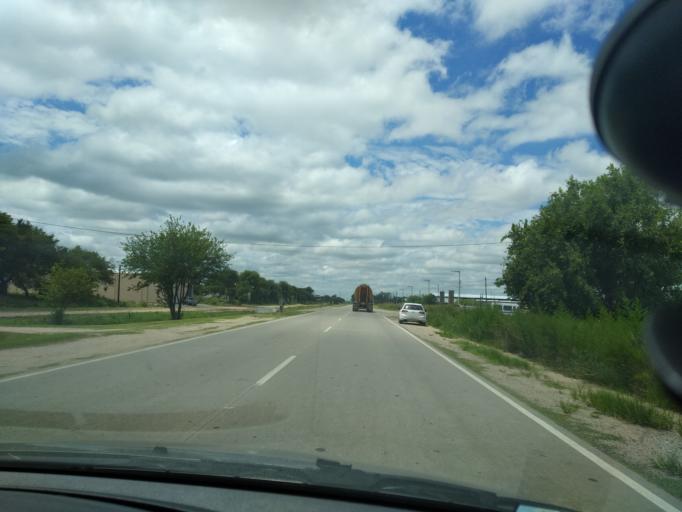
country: AR
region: Cordoba
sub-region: Departamento de Rio Segundo
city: Rio Segundo
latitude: -31.6420
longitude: -63.8971
